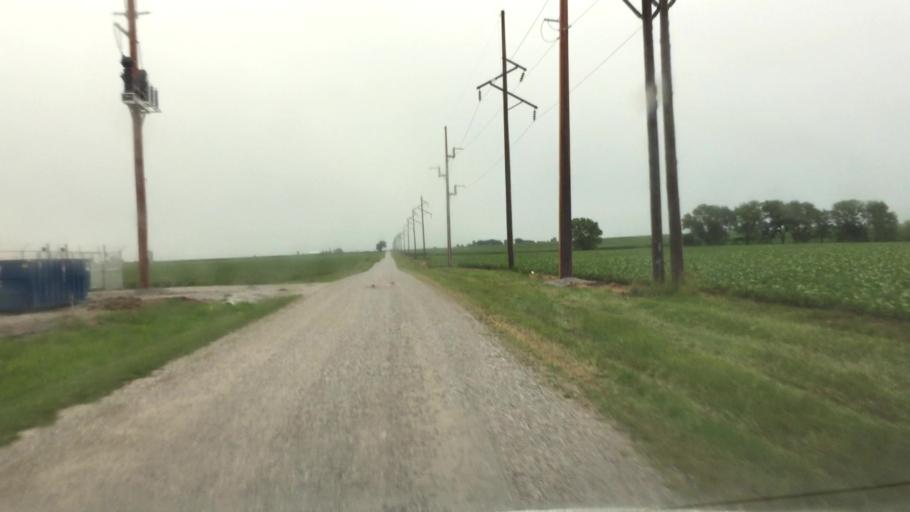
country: US
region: Illinois
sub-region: Hancock County
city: Hamilton
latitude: 40.4248
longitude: -91.2709
